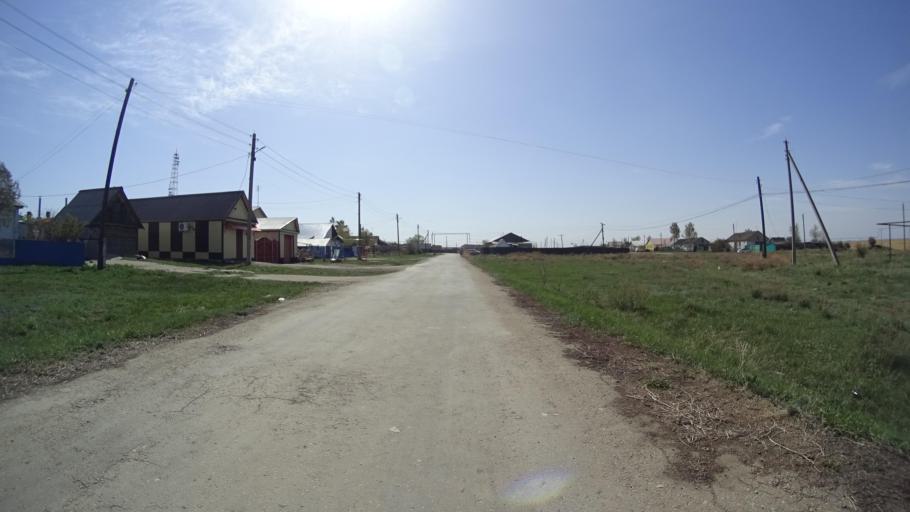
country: RU
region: Chelyabinsk
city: Chesma
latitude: 53.7909
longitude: 61.0374
